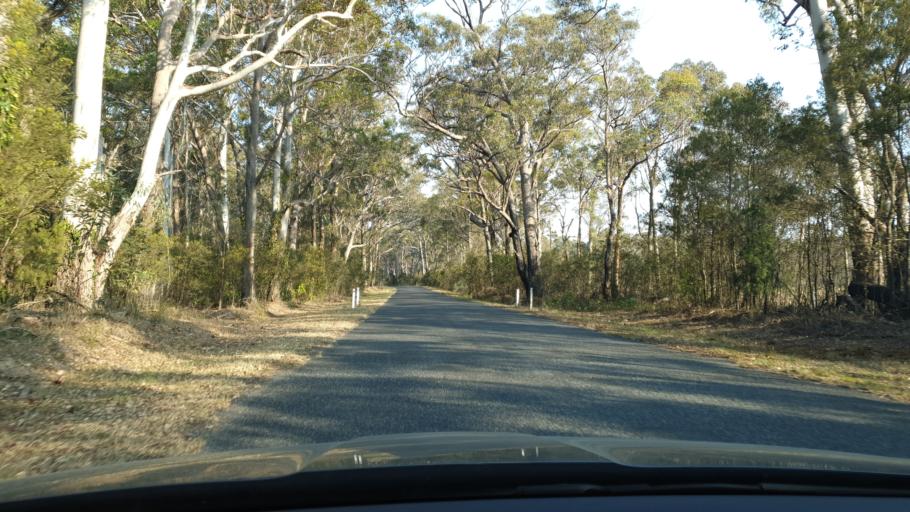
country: AU
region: New South Wales
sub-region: Tenterfield Municipality
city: Carrolls Creek
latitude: -28.6977
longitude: 152.0935
